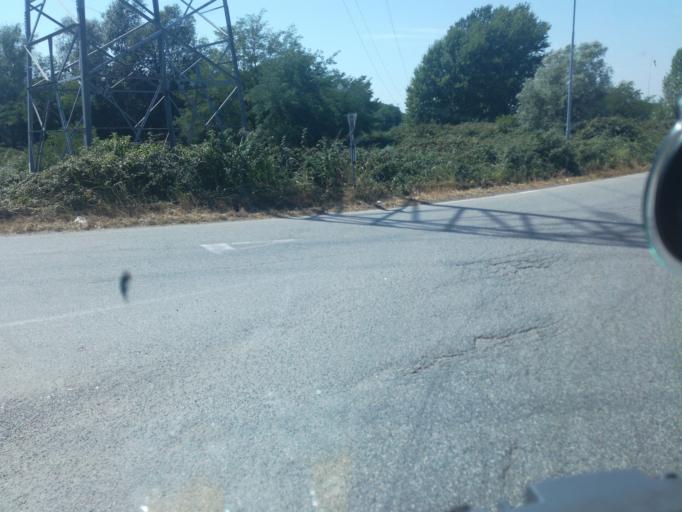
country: IT
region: Piedmont
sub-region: Provincia di Novara
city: Pernate
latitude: 45.4620
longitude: 8.6524
